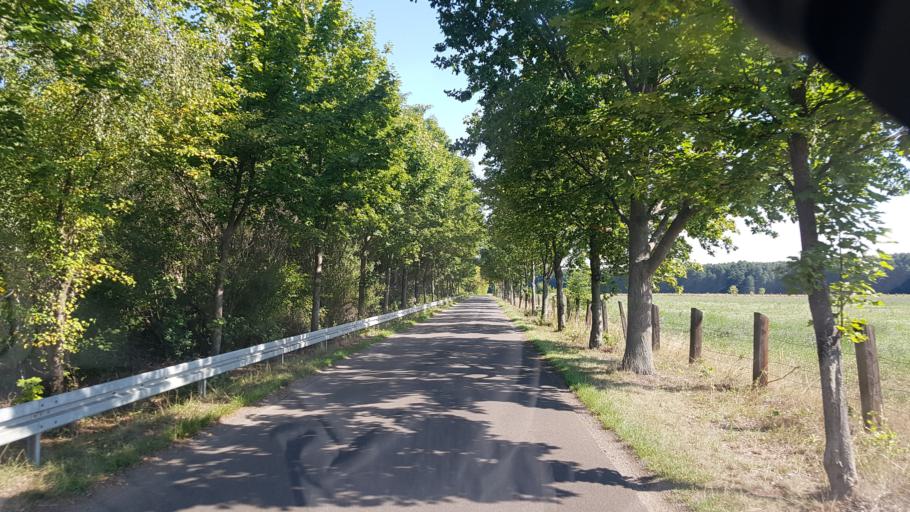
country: DE
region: Brandenburg
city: Vetschau
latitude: 51.7571
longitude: 14.0414
